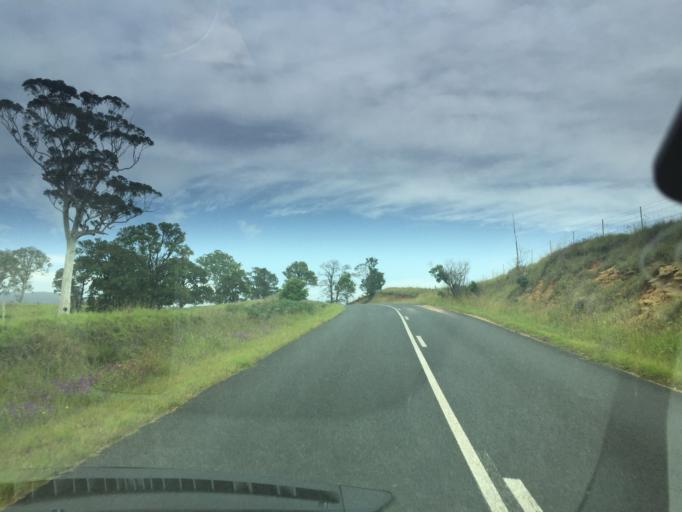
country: AU
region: New South Wales
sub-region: Bega Valley
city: Bega
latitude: -36.7233
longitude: 149.6082
